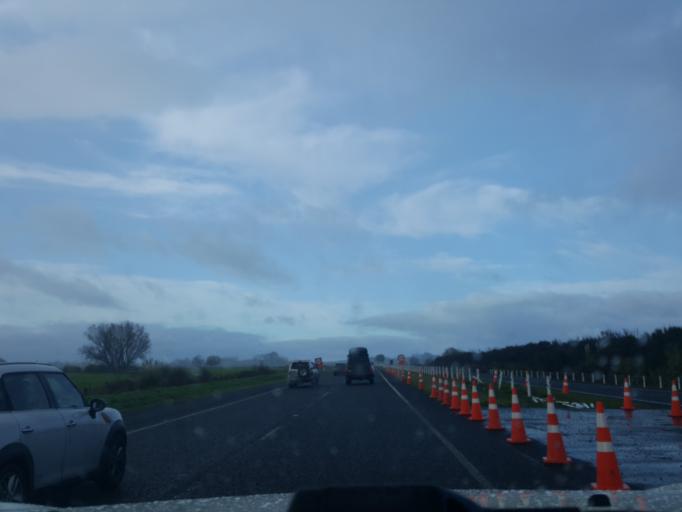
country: NZ
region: Waikato
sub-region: Waikato District
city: Ngaruawahia
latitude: -37.6507
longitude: 175.2060
